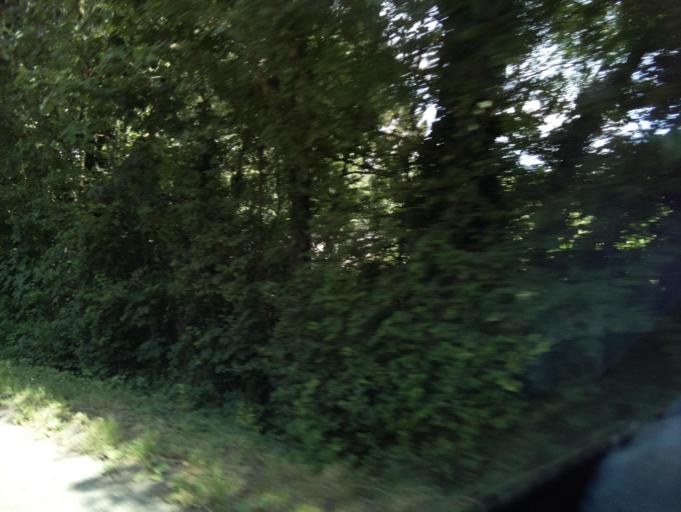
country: GB
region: England
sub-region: Wiltshire
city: Malmesbury
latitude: 51.5714
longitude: -2.0744
